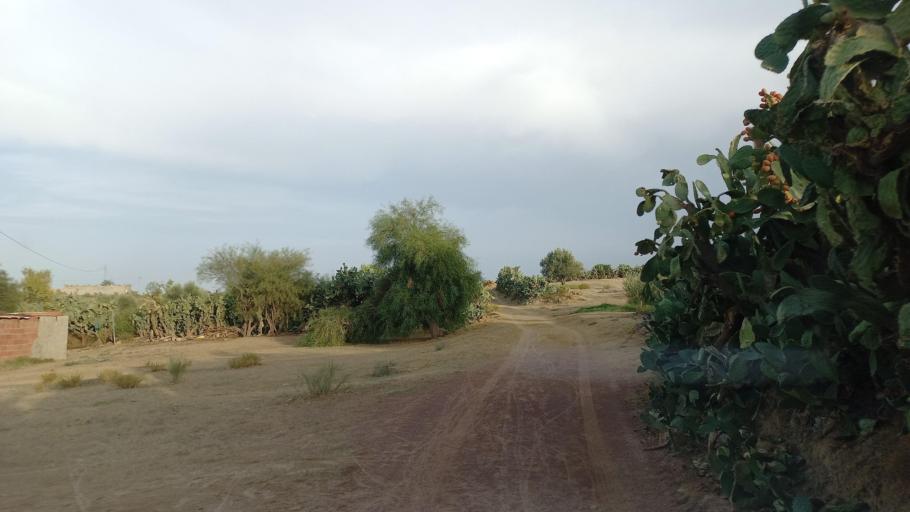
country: TN
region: Al Qasrayn
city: Kasserine
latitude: 35.2172
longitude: 9.0551
